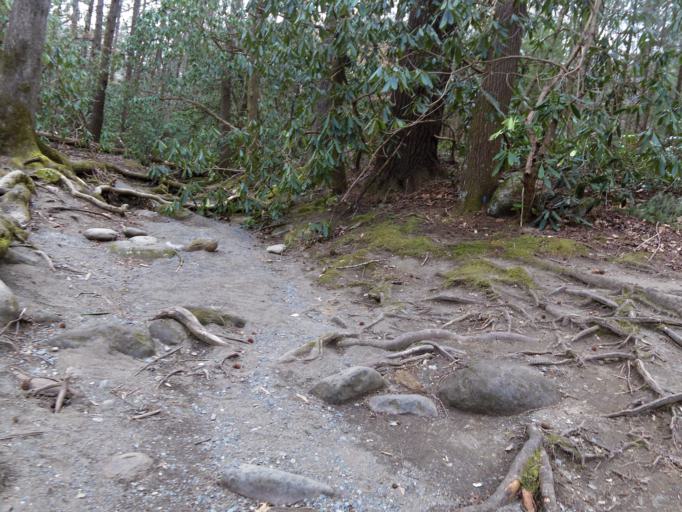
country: US
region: Tennessee
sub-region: Sevier County
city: Gatlinburg
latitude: 35.6790
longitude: -83.5292
